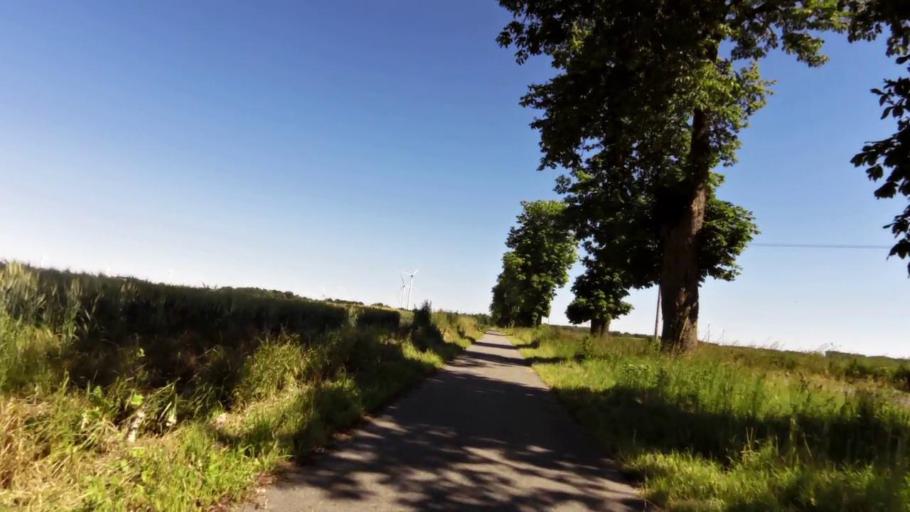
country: PL
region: West Pomeranian Voivodeship
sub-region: Powiat kolobrzeski
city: Dygowo
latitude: 54.0468
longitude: 15.7644
